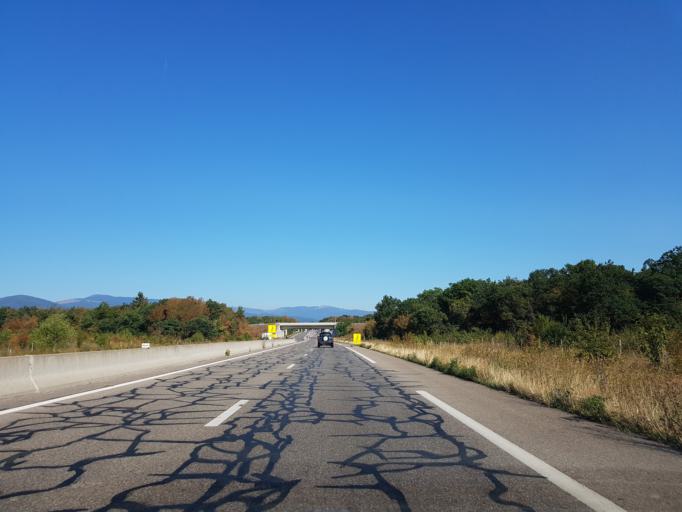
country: FR
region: Alsace
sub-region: Departement du Haut-Rhin
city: Pulversheim
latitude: 47.8172
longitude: 7.2956
